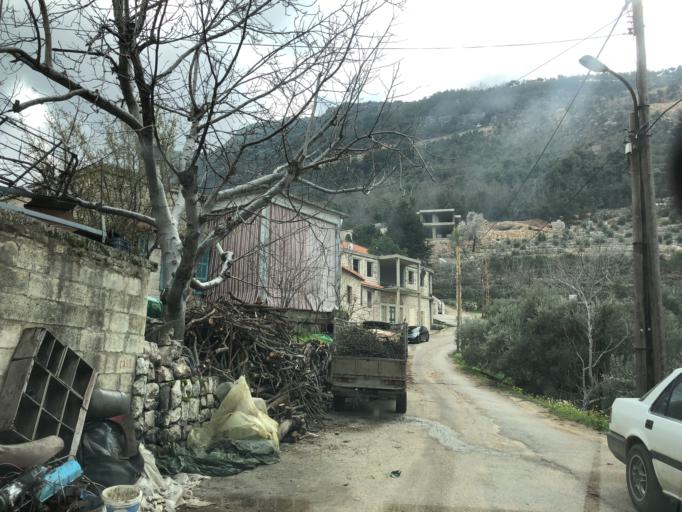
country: LB
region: Liban-Nord
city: Amioun
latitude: 34.2050
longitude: 35.8382
